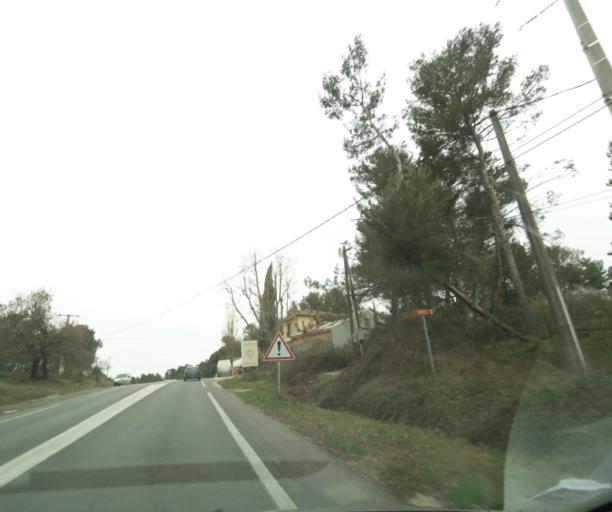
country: FR
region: Provence-Alpes-Cote d'Azur
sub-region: Departement des Bouches-du-Rhone
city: Fuveau
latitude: 43.4543
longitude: 5.5454
